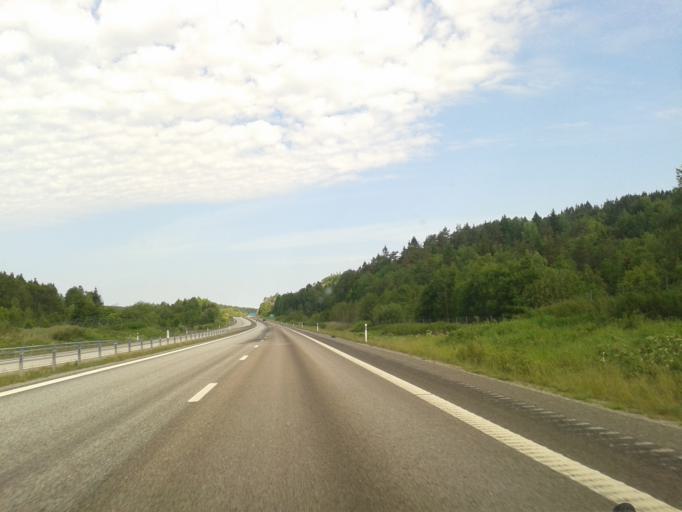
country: SE
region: Vaestra Goetaland
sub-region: Lysekils Kommun
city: Brastad
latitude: 58.5514
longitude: 11.5058
